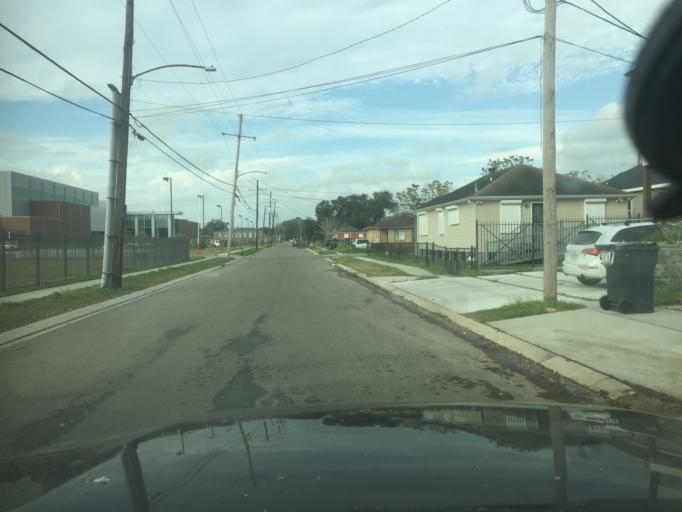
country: US
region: Louisiana
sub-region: Orleans Parish
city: New Orleans
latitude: 29.9960
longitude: -90.0818
